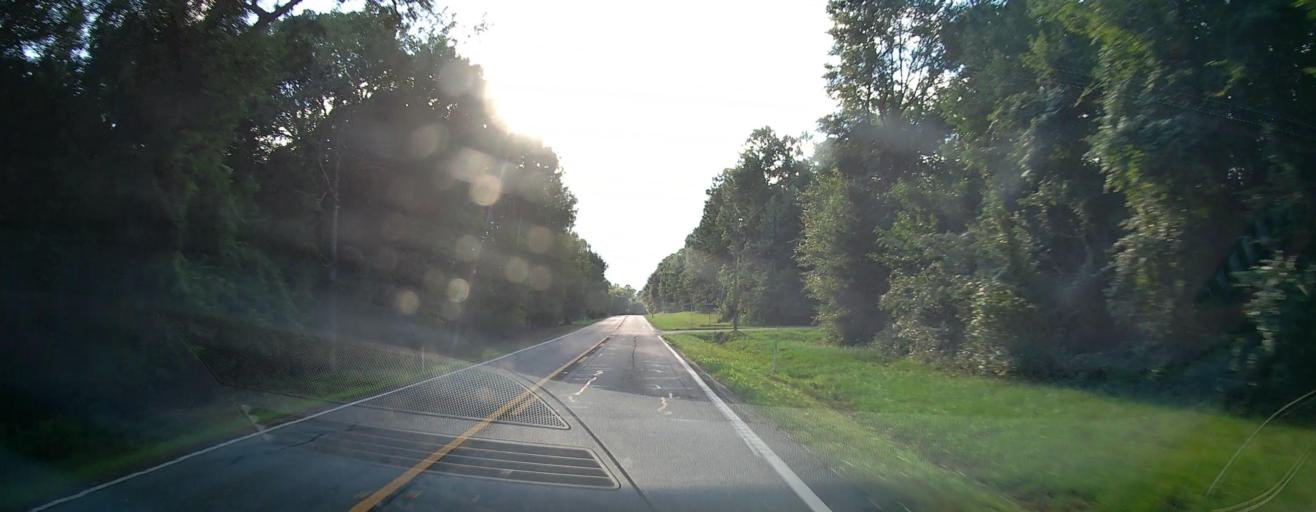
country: US
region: Georgia
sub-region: Pulaski County
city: Hawkinsville
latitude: 32.2667
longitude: -83.5326
